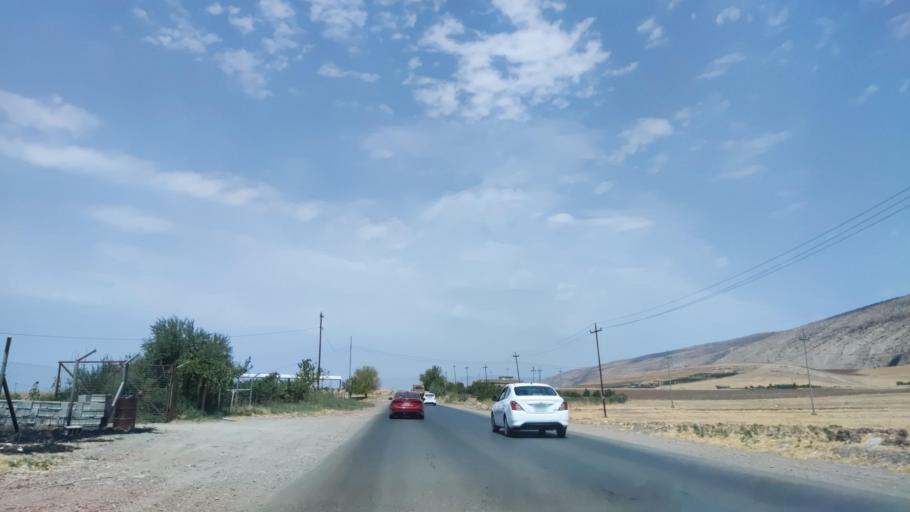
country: IQ
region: Arbil
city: Shaqlawah
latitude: 36.5142
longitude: 44.3739
